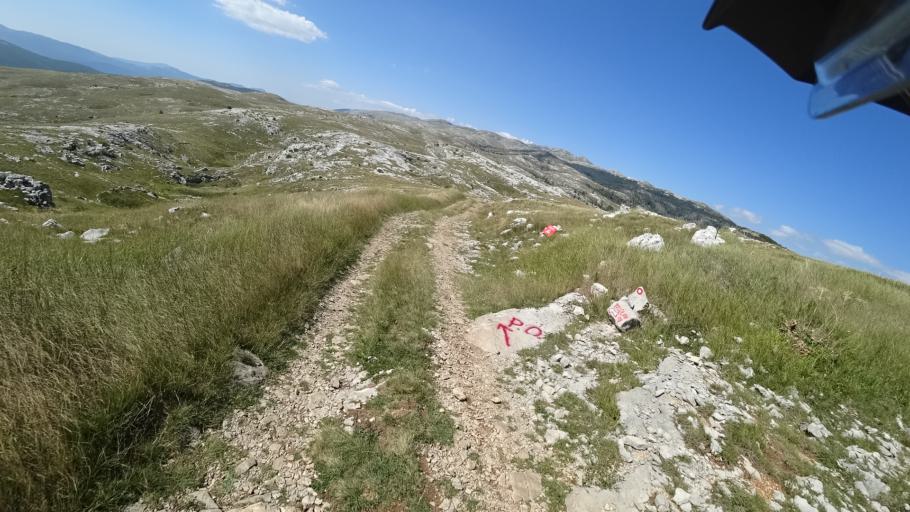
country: HR
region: Splitsko-Dalmatinska
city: Hrvace
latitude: 43.8927
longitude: 16.6341
